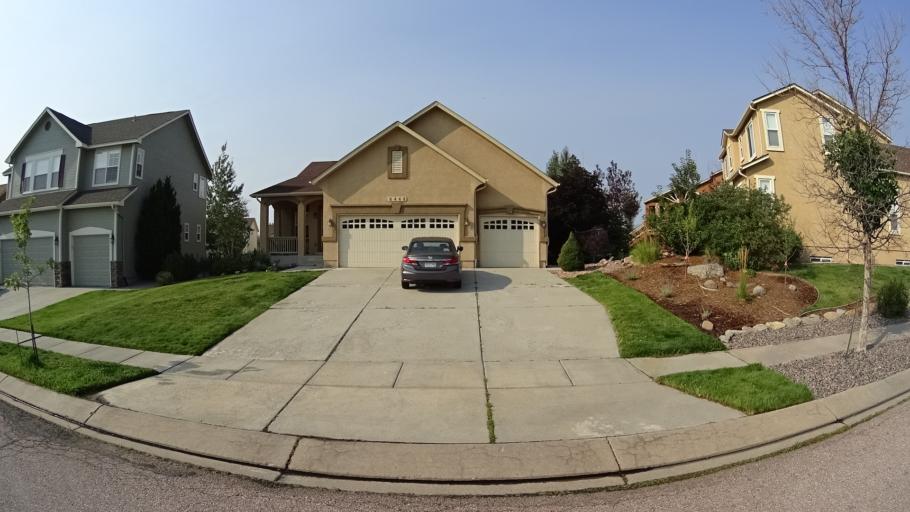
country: US
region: Colorado
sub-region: El Paso County
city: Black Forest
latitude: 38.9541
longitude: -104.7209
